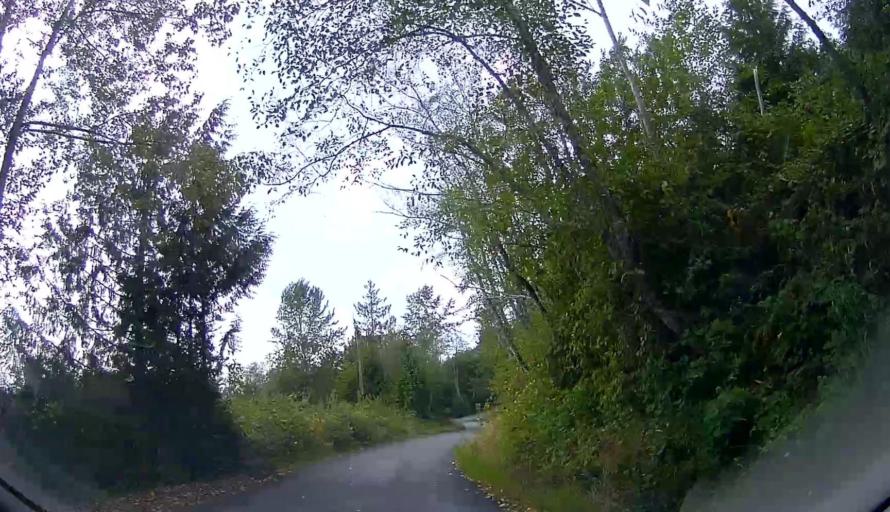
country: US
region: Washington
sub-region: Skagit County
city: Burlington
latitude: 48.5914
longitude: -122.3991
